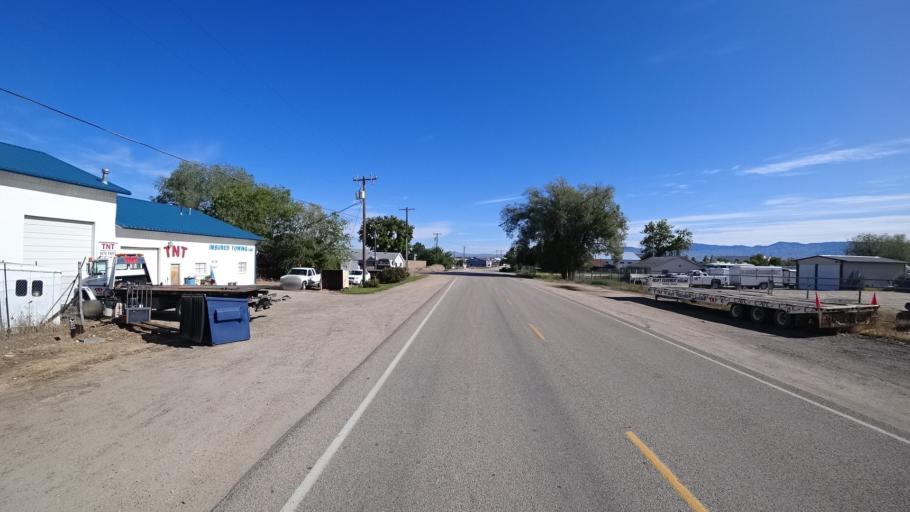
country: US
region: Idaho
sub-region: Ada County
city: Garden City
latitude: 43.5667
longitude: -116.2598
